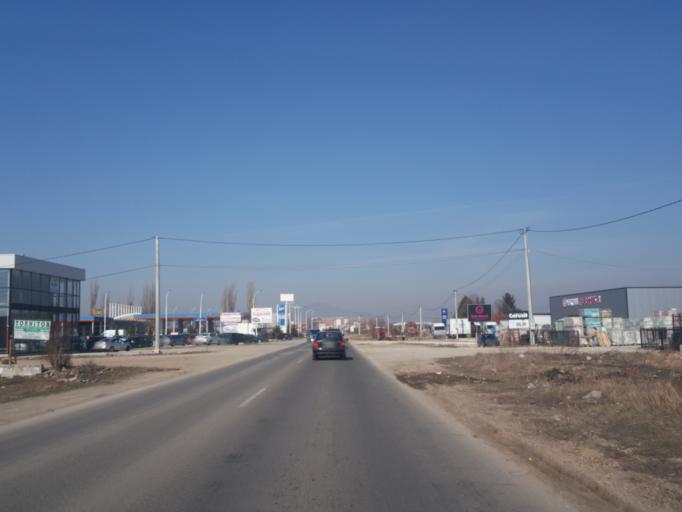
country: XK
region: Mitrovica
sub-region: Vushtrri
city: Vushtrri
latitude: 42.8077
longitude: 20.9892
